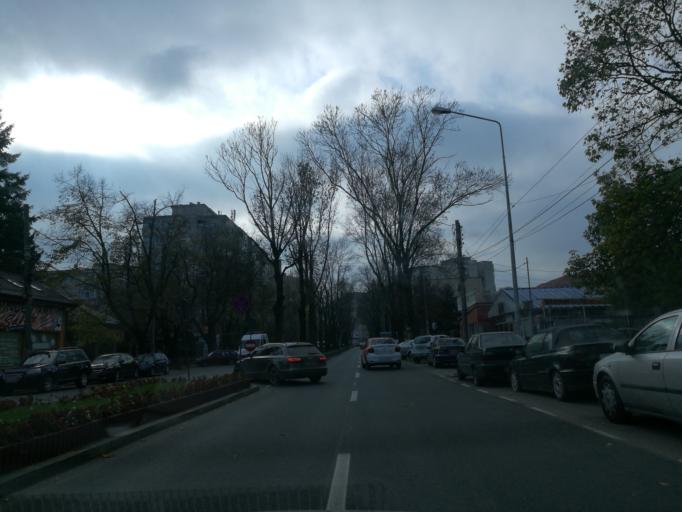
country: RO
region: Ilfov
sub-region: Comuna Chiajna
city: Rosu
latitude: 44.4366
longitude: 26.0134
